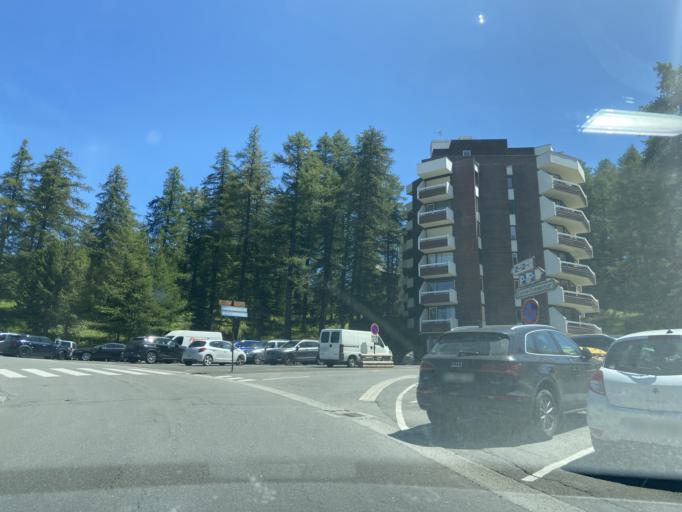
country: FR
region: Provence-Alpes-Cote d'Azur
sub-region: Departement des Hautes-Alpes
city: Guillestre
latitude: 44.5692
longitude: 6.6831
